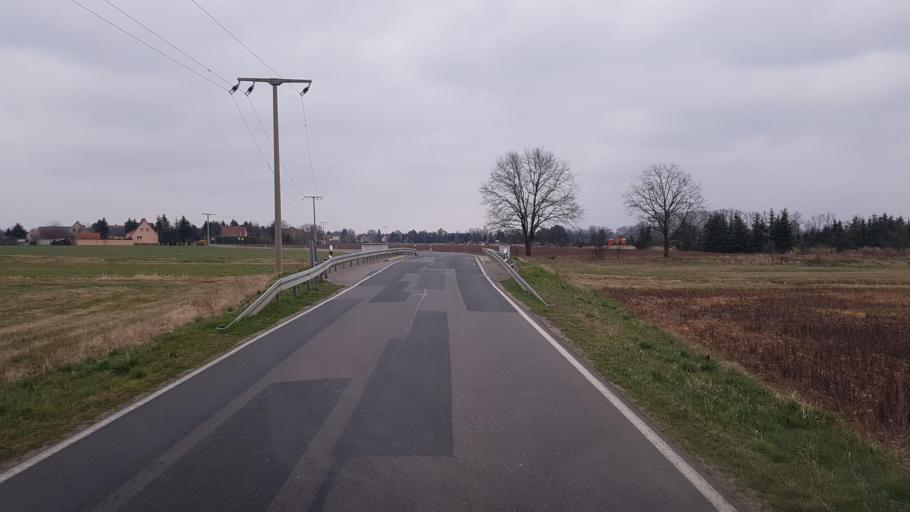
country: DE
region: Saxony
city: Nauwalde
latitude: 51.4187
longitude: 13.4273
